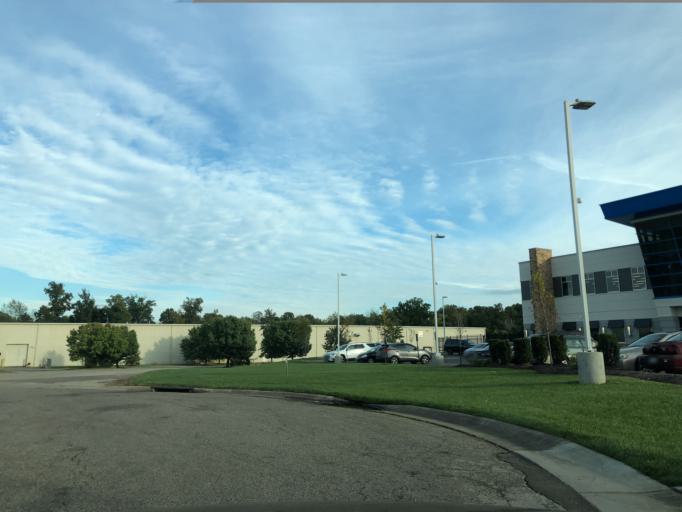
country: US
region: Ohio
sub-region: Hamilton County
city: Sixteen Mile Stand
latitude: 39.2790
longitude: -84.3013
